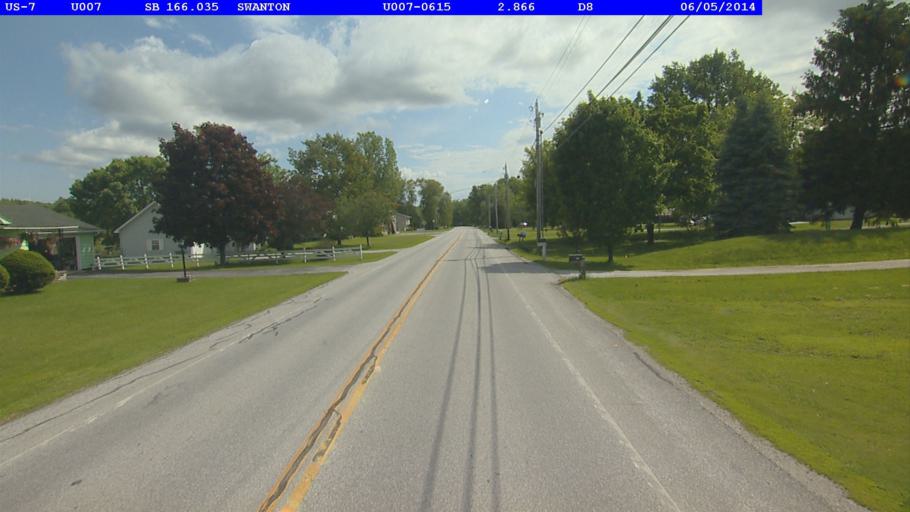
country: US
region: Vermont
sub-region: Franklin County
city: Swanton
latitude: 44.8876
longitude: -73.0914
